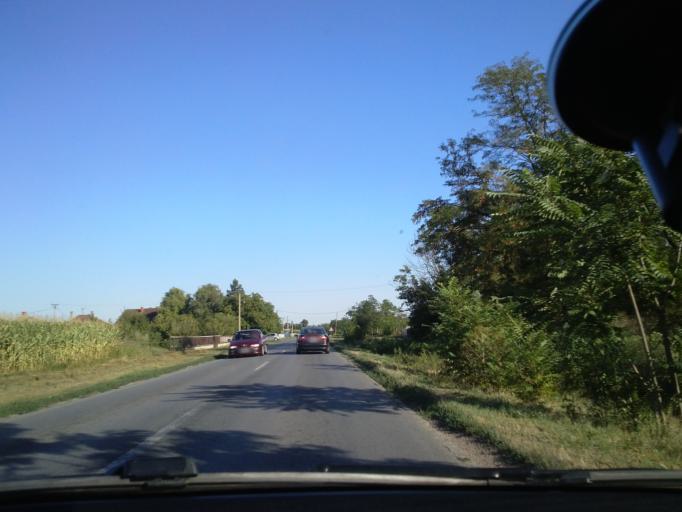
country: RS
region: Autonomna Pokrajina Vojvodina
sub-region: Zapadnobacki Okrug
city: Sombor
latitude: 45.7312
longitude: 19.1463
